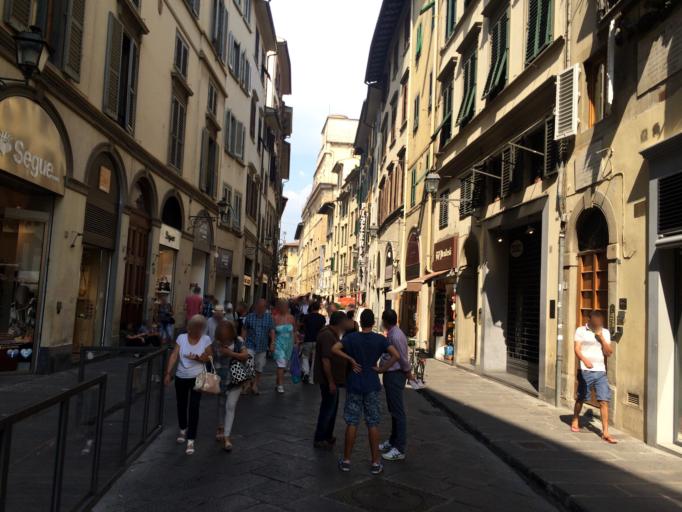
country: IT
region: Tuscany
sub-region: Province of Florence
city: Florence
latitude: 43.7741
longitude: 11.2548
